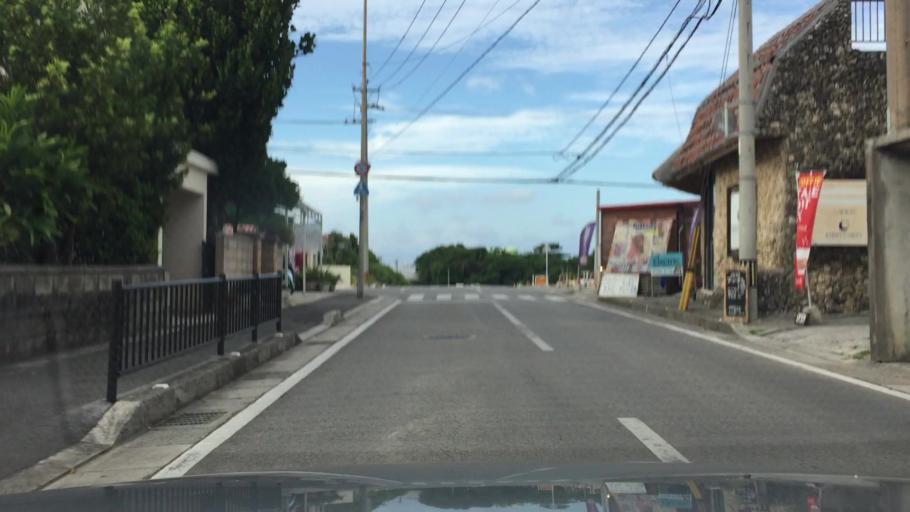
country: JP
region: Okinawa
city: Ishigaki
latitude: 24.4611
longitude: 124.1420
